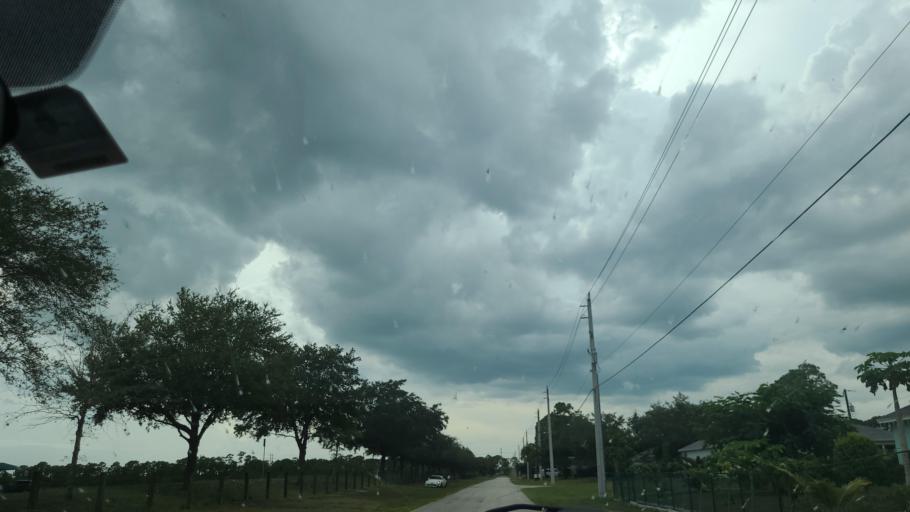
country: US
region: Florida
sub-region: Saint Lucie County
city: Port Saint Lucie
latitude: 27.2499
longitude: -80.4090
